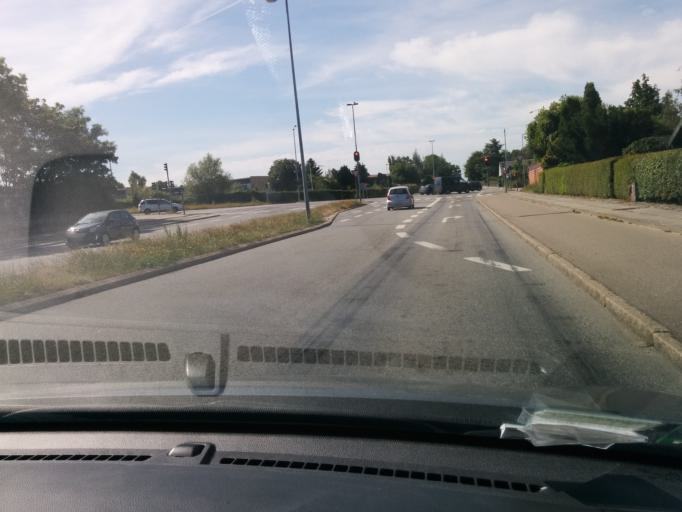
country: DK
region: Central Jutland
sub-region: Arhus Kommune
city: Arhus
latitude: 56.1747
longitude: 10.1659
